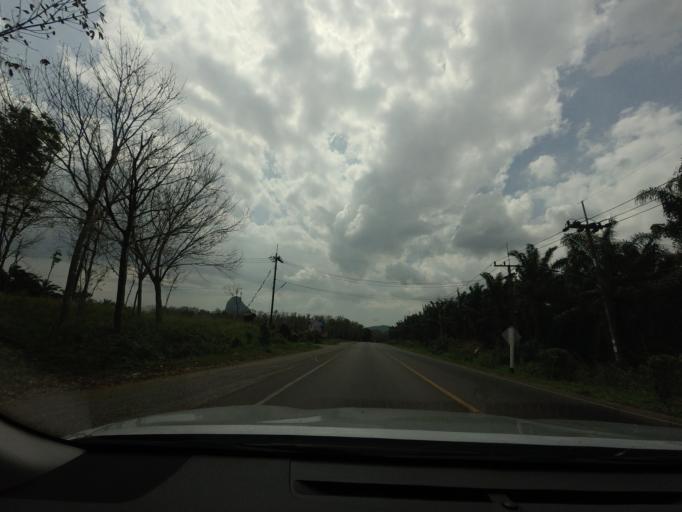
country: TH
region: Phangnga
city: Ban Ao Nang
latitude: 8.1279
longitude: 98.8061
